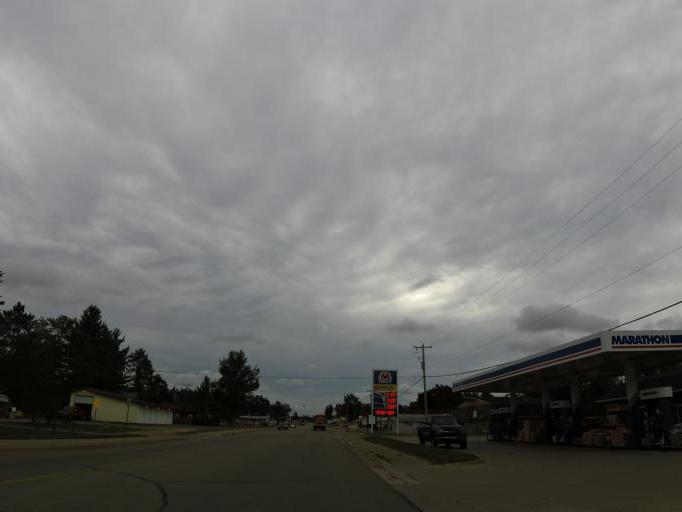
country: US
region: Michigan
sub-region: Roscommon County
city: Saint Helen
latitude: 44.3599
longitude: -84.4103
